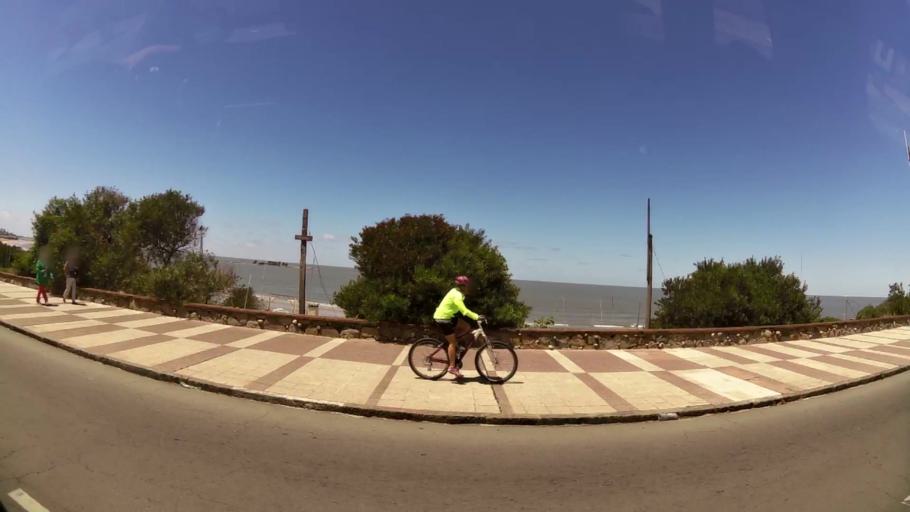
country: UY
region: Canelones
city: Paso de Carrasco
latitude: -34.8966
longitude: -56.1125
